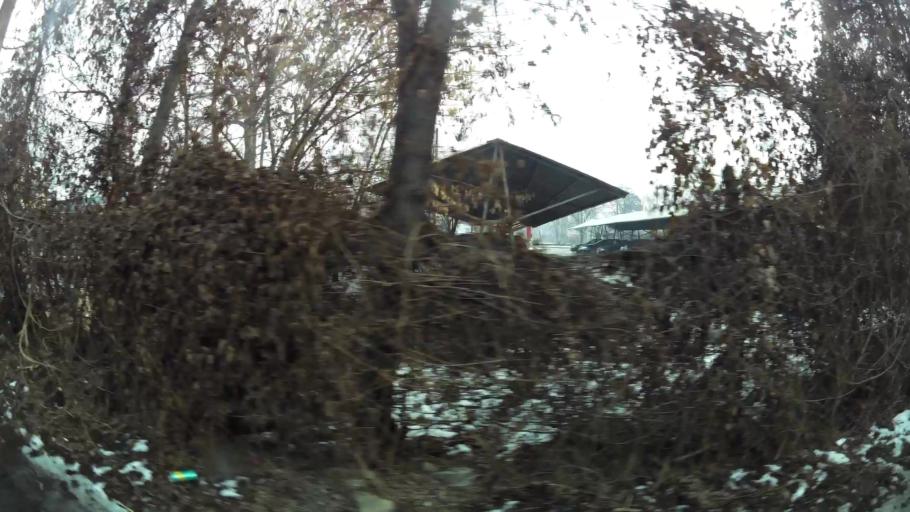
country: MK
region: Karpos
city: Skopje
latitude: 41.9940
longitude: 21.4548
